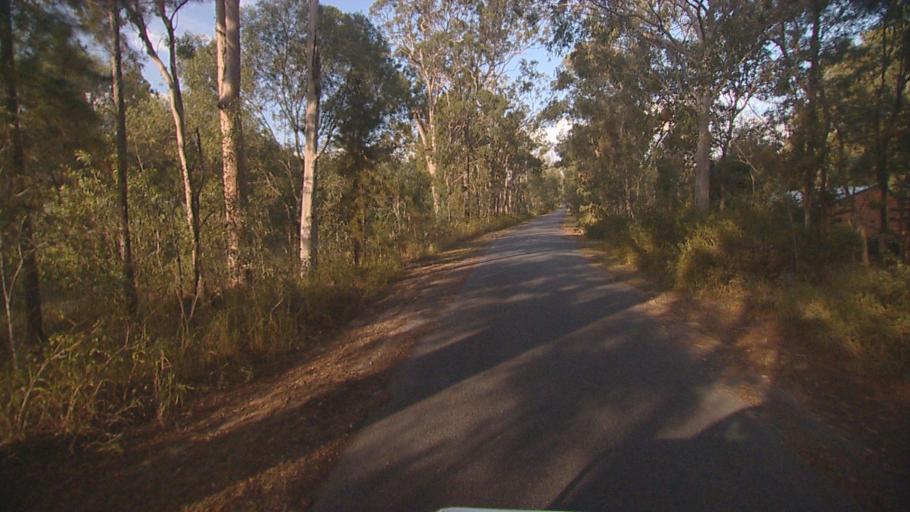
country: AU
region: Queensland
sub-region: Logan
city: Chambers Flat
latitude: -27.8378
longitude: 153.1127
